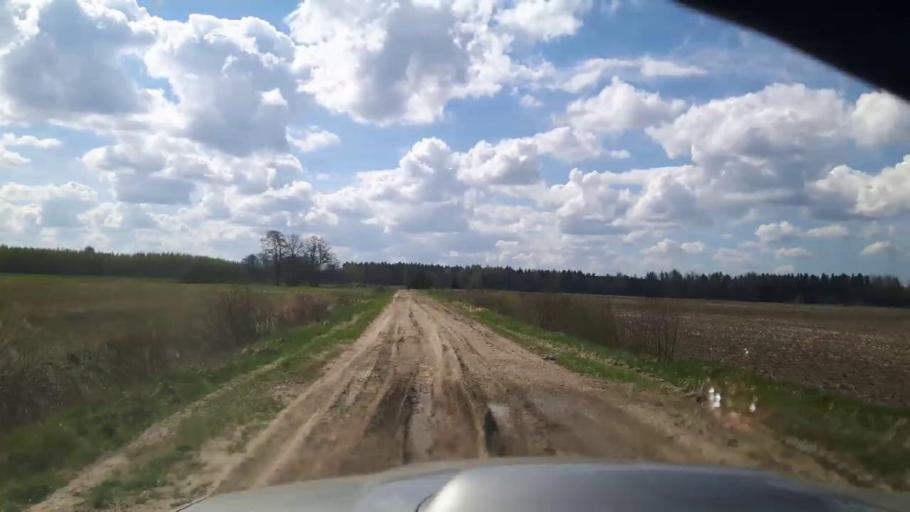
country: EE
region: Paernumaa
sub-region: Vaendra vald (alev)
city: Vandra
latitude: 58.5422
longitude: 25.0699
